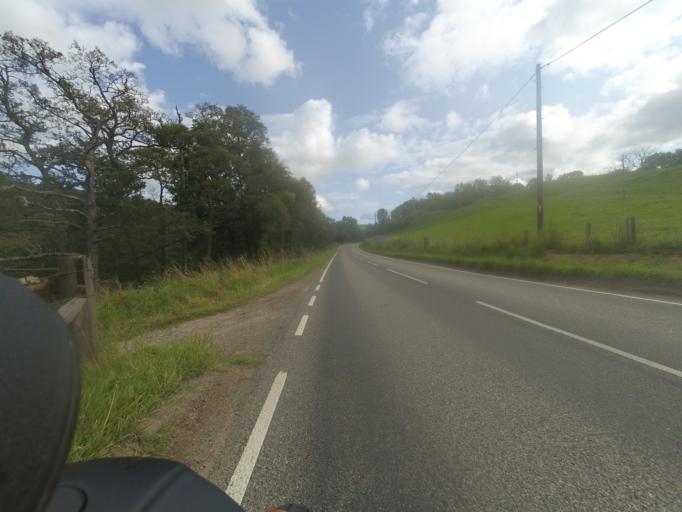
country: GB
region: Scotland
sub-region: Moray
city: Dufftown
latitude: 57.4439
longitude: -3.1160
